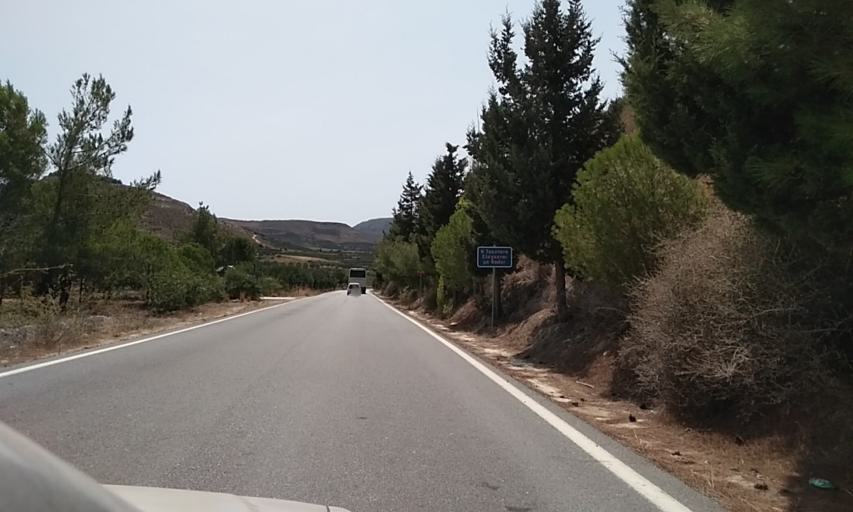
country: GR
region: Crete
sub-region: Nomos Lasithiou
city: Siteia
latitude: 35.1075
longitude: 26.0592
